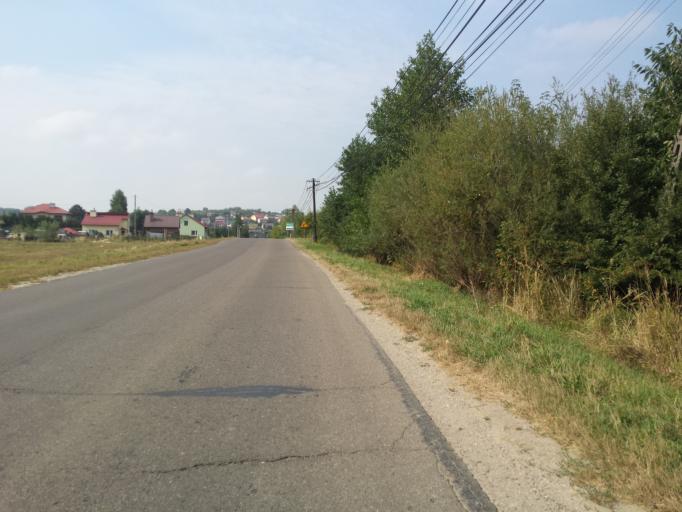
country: PL
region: Subcarpathian Voivodeship
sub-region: Powiat rzeszowski
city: Blazowa
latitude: 49.8770
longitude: 22.0973
